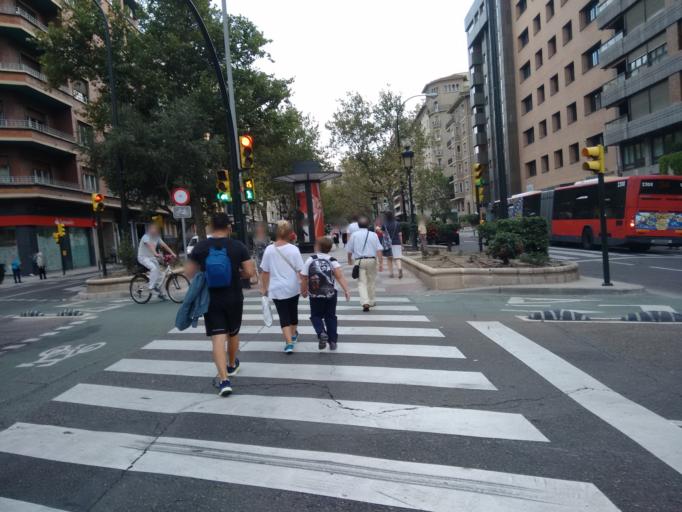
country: ES
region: Aragon
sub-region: Provincia de Zaragoza
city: Zaragoza
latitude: 41.6422
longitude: -0.8861
